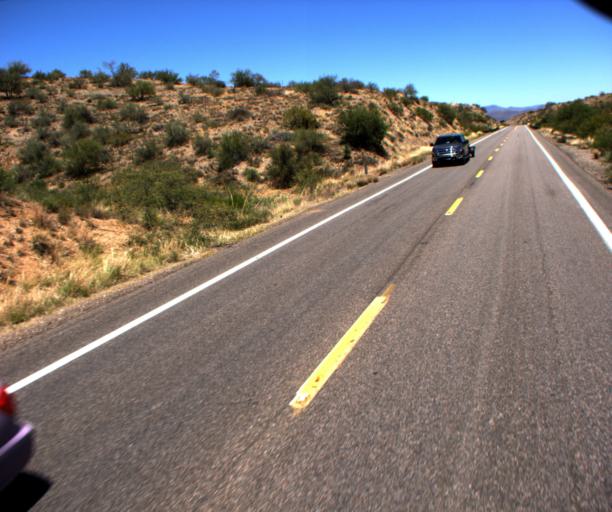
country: US
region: Arizona
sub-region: Gila County
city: Globe
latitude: 33.3196
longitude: -110.7353
